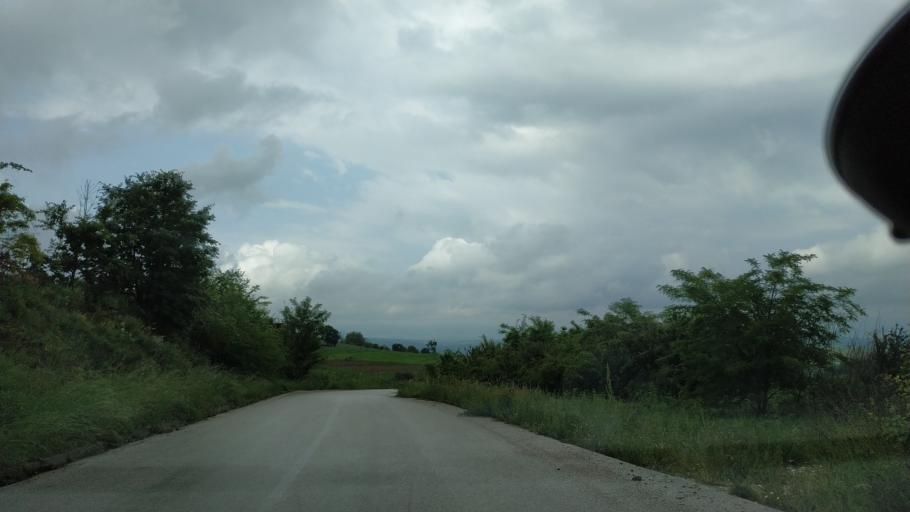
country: RS
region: Central Serbia
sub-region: Toplicki Okrug
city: Prokuplje
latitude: 43.4163
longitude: 21.5534
